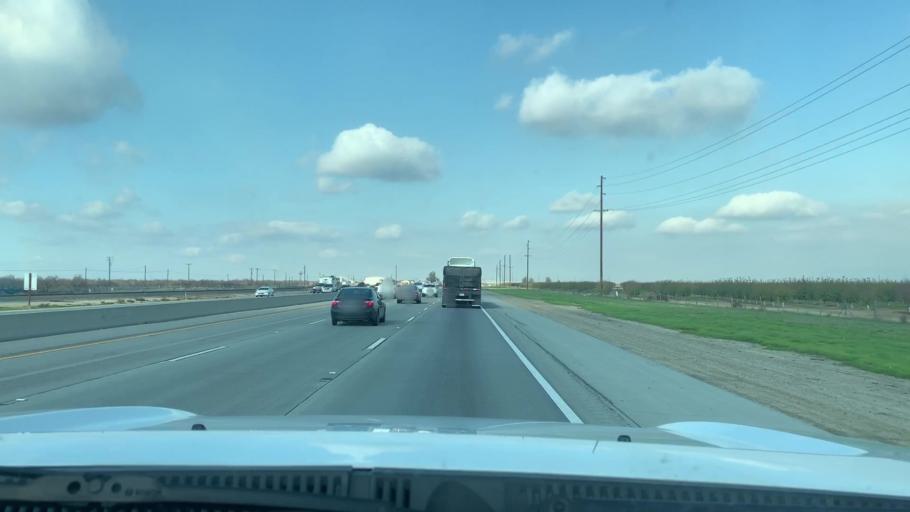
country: US
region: California
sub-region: Kern County
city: Shafter
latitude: 35.5472
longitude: -119.1953
